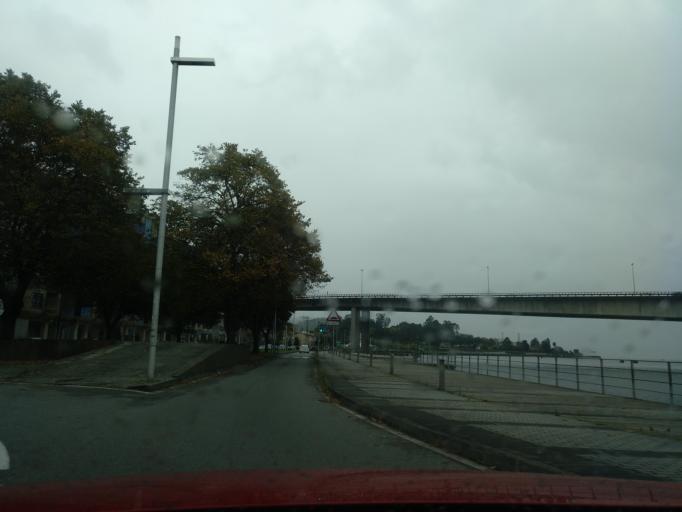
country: ES
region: Galicia
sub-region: Provincia de Pontevedra
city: Poio
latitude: 42.4271
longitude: -8.6526
